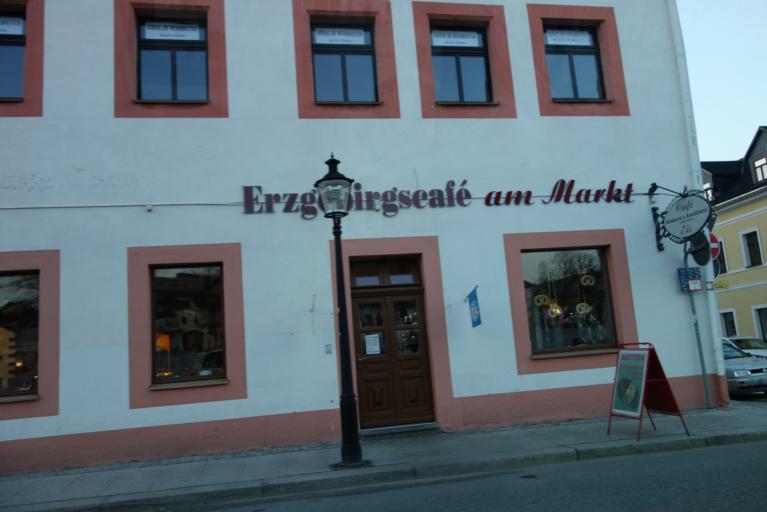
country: DE
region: Saxony
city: Marienberg
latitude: 50.6508
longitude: 13.1643
